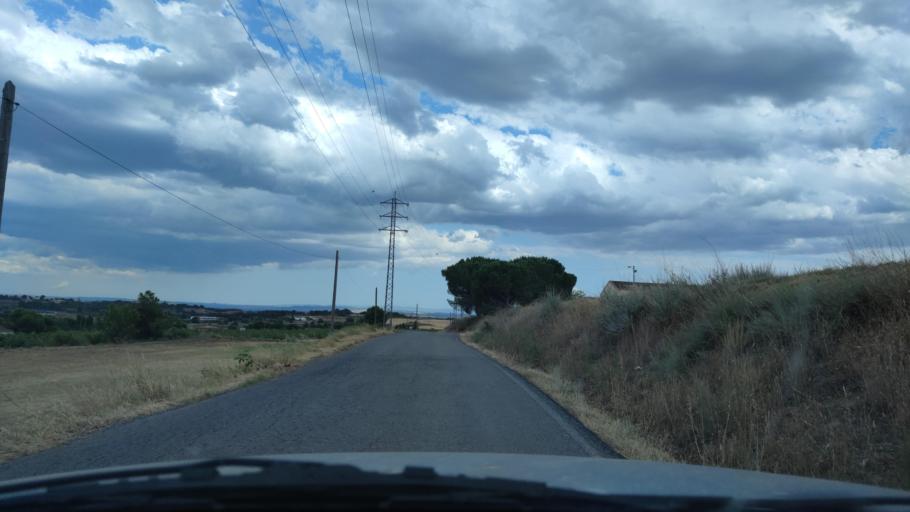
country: ES
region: Catalonia
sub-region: Provincia de Lleida
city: Lleida
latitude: 41.6140
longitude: 0.5787
